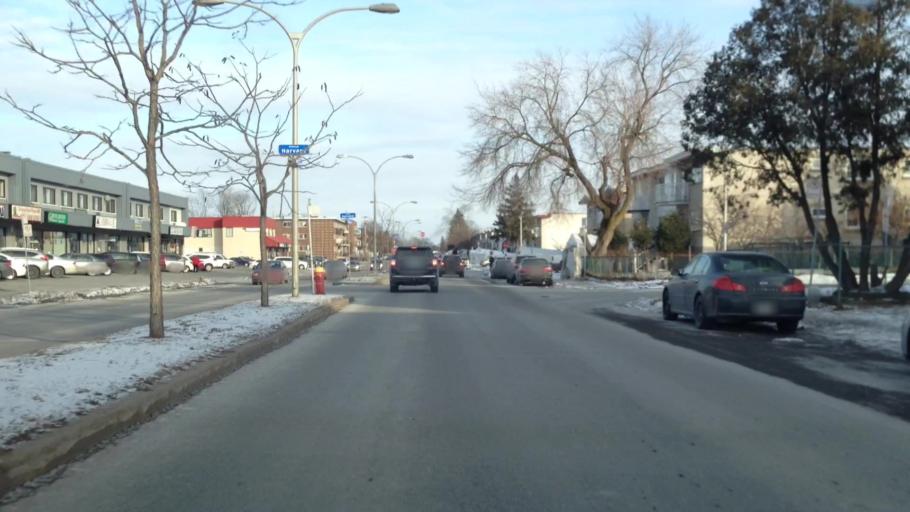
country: CA
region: Quebec
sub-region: Laval
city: Laval
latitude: 45.5377
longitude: -73.7583
